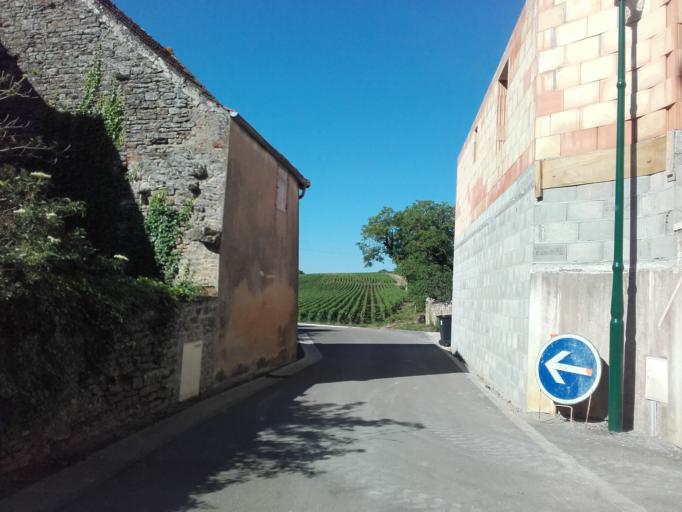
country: FR
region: Bourgogne
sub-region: Departement de la Cote-d'Or
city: Nolay
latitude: 46.9125
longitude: 4.6818
